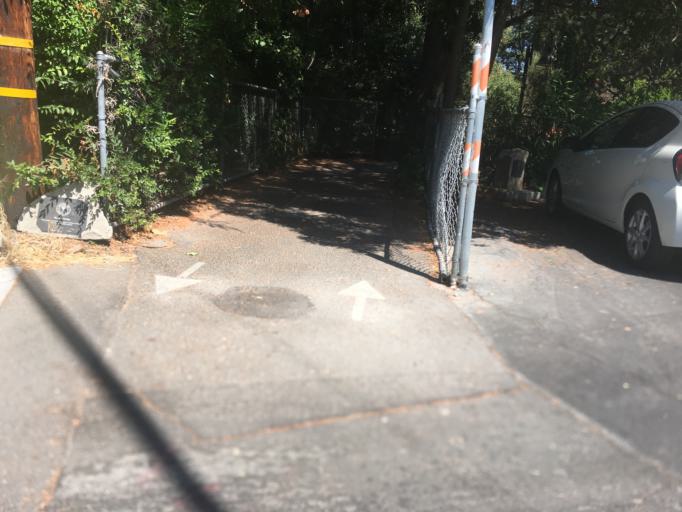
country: US
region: California
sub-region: Santa Clara County
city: Los Altos
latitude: 37.4092
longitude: -122.1183
